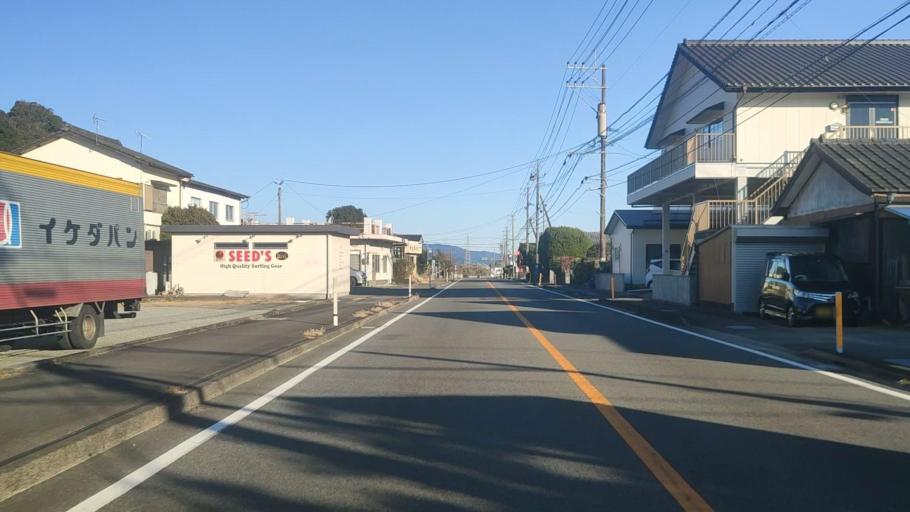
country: JP
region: Miyazaki
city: Nobeoka
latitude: 32.3857
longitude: 131.6275
